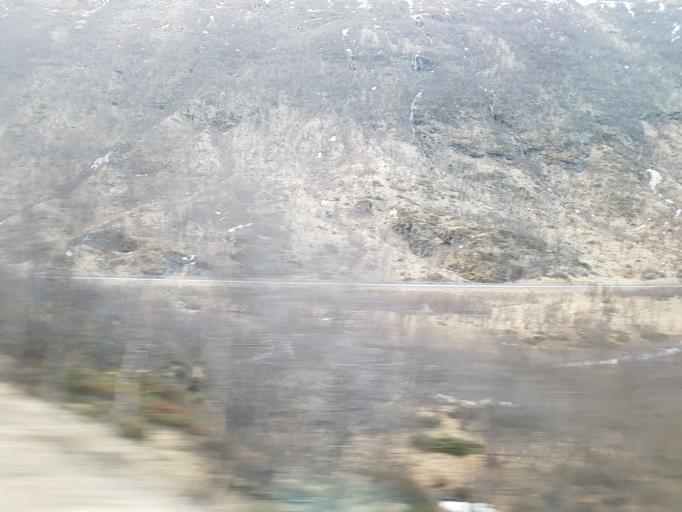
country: NO
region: Sor-Trondelag
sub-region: Oppdal
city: Oppdal
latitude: 62.3293
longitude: 9.6180
